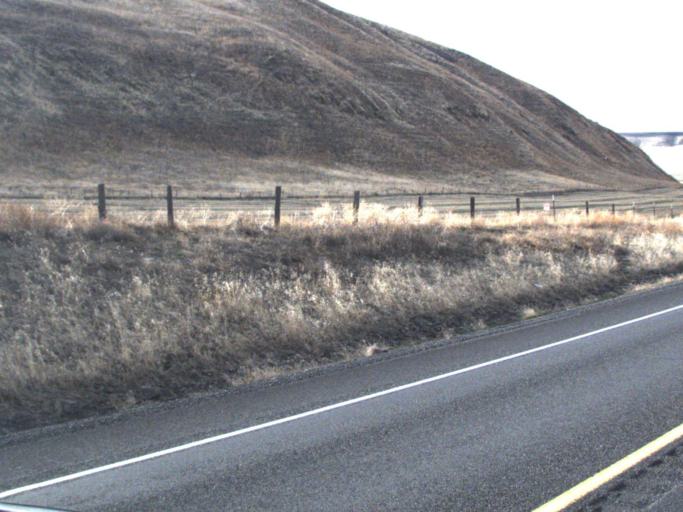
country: US
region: Washington
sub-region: Columbia County
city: Dayton
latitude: 46.5449
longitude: -117.8730
